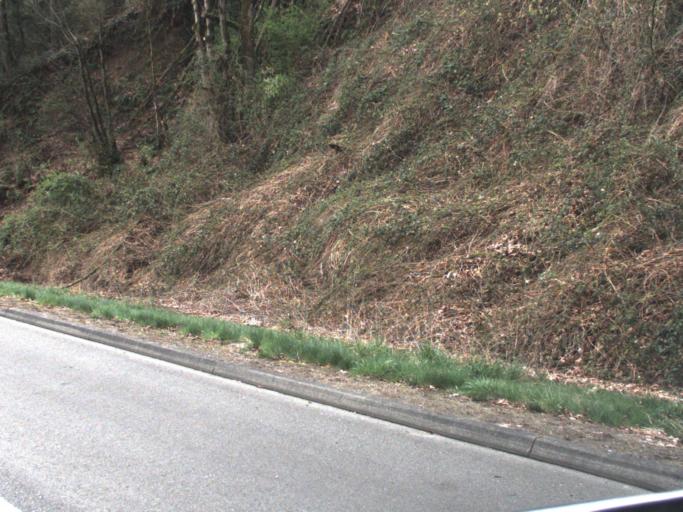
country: US
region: Washington
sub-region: King County
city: Kent
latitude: 47.3858
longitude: -122.2776
